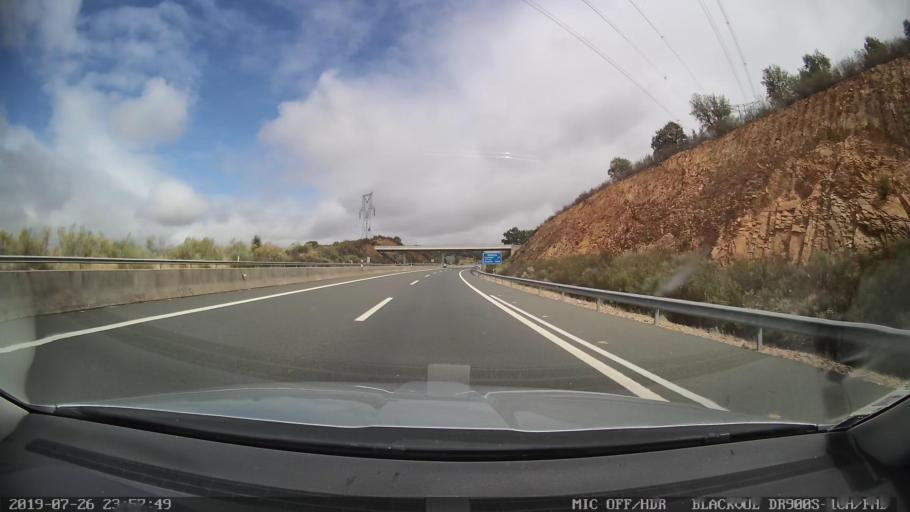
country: ES
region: Extremadura
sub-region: Provincia de Caceres
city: Casas de Miravete
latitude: 39.7368
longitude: -5.7238
